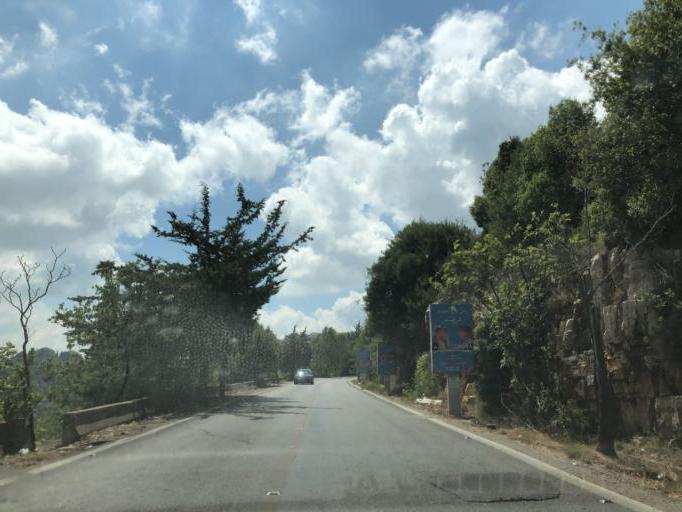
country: LB
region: Mont-Liban
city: Beit ed Dine
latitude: 33.7007
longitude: 35.5910
